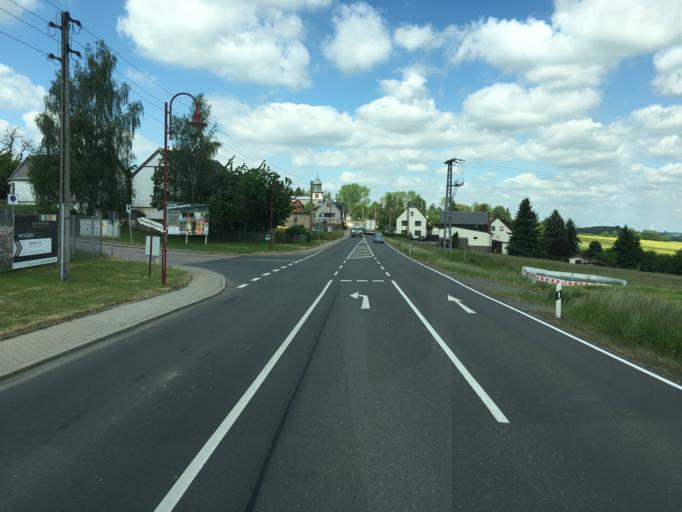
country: DE
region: Saxony
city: Hainichen
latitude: 50.9991
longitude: 13.1244
